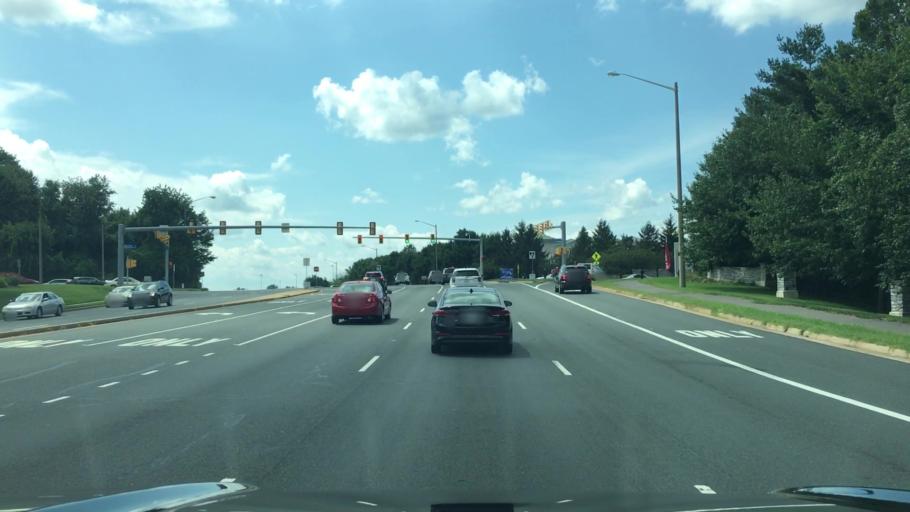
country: US
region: Virginia
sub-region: Fairfax County
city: Centreville
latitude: 38.8387
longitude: -77.4399
